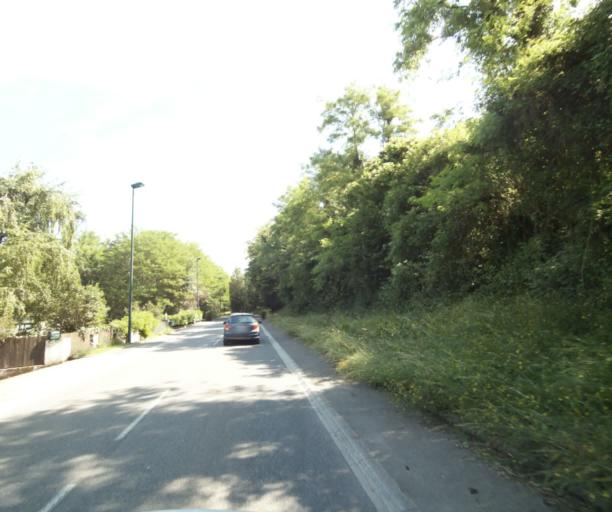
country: FR
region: Rhone-Alpes
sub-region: Departement de la Haute-Savoie
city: Margencel
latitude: 46.3443
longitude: 6.4380
